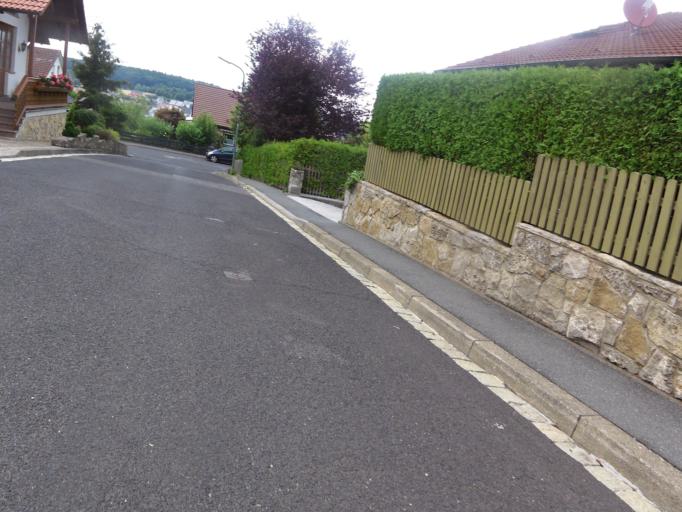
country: DE
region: Bavaria
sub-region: Regierungsbezirk Unterfranken
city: Hochberg
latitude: 49.7749
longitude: 9.8741
